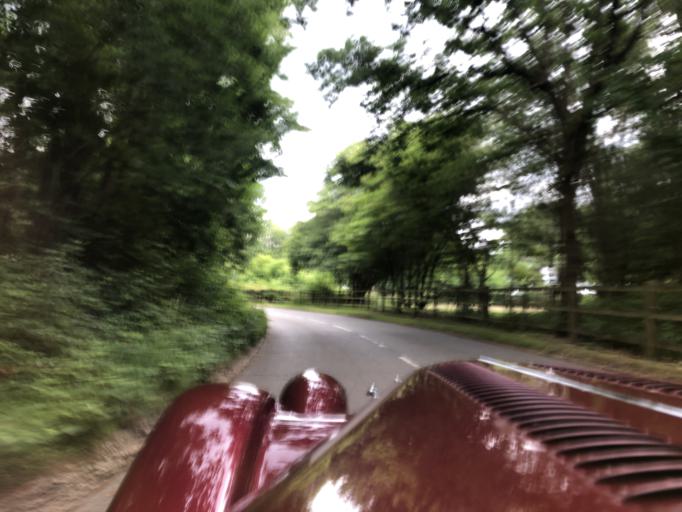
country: GB
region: England
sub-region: East Sussex
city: Wadhurst
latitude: 51.0833
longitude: 0.3948
